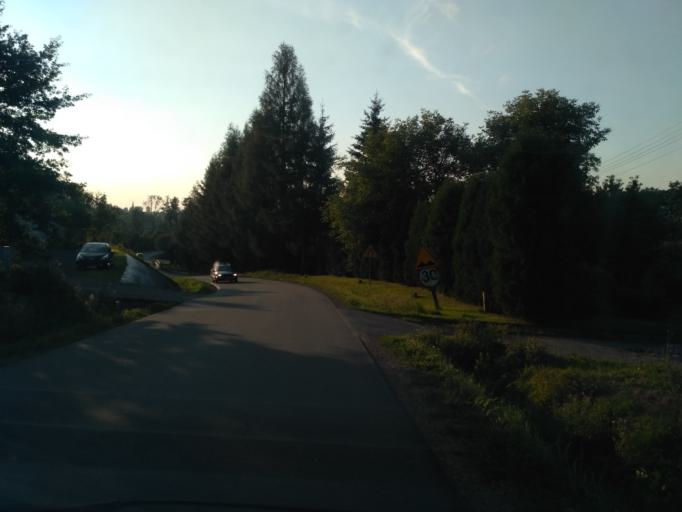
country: PL
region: Subcarpathian Voivodeship
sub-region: Powiat krosnienski
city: Korczyna
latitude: 49.7059
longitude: 21.8317
